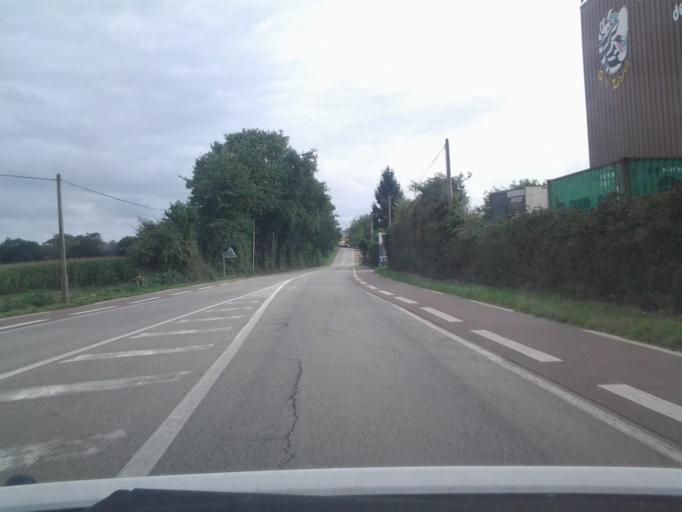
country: FR
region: Pays de la Loire
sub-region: Departement de la Vendee
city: La Roche-sur-Yon
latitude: 46.6889
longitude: -1.4243
